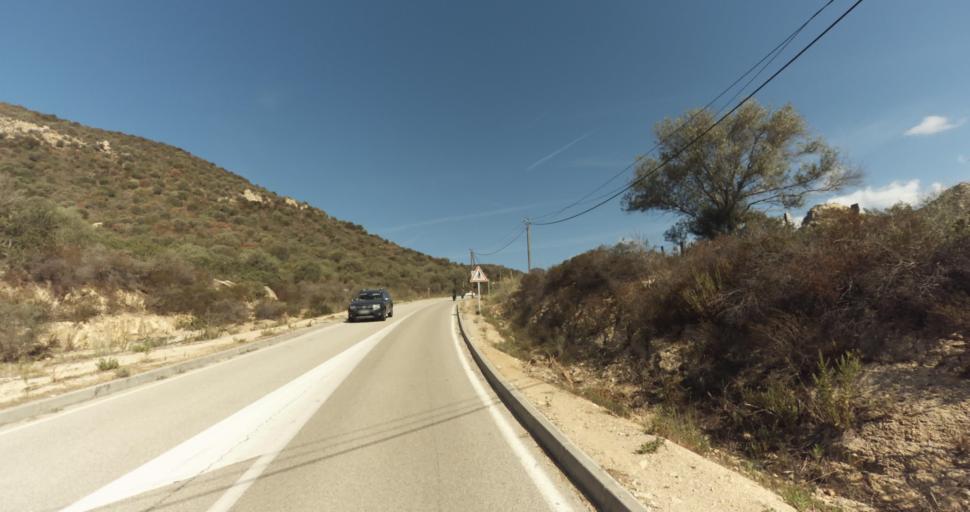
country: FR
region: Corsica
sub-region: Departement de la Corse-du-Sud
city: Ajaccio
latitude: 41.9121
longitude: 8.6439
